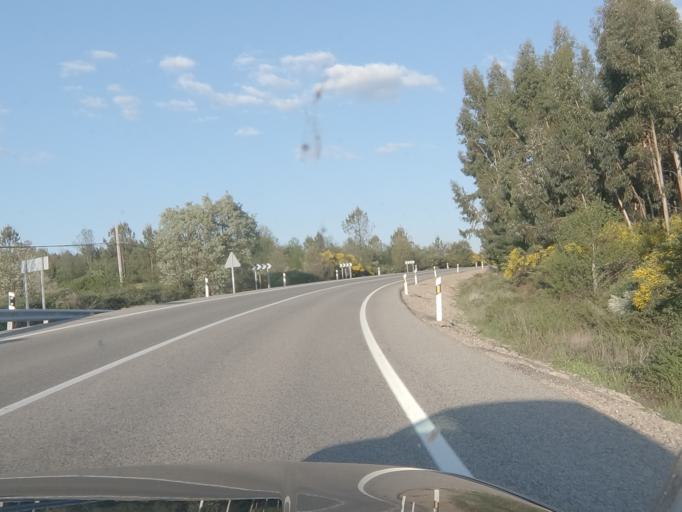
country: PT
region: Portalegre
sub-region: Portalegre
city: Sao Juliao
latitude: 39.3427
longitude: -7.2834
